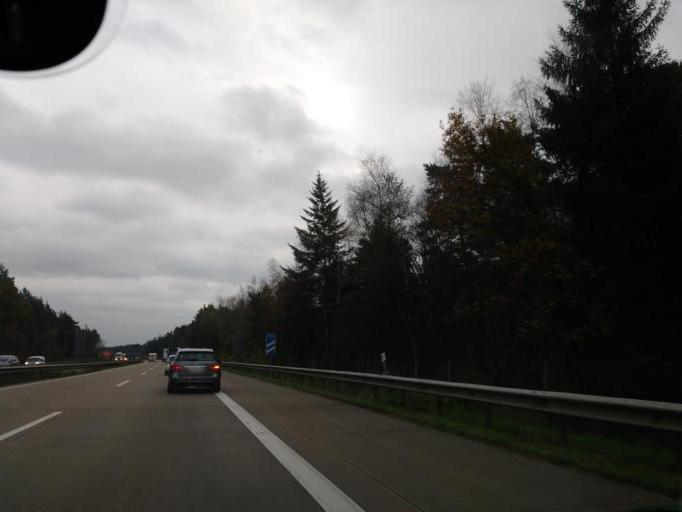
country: DE
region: Lower Saxony
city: Verden
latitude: 52.9365
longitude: 9.2733
